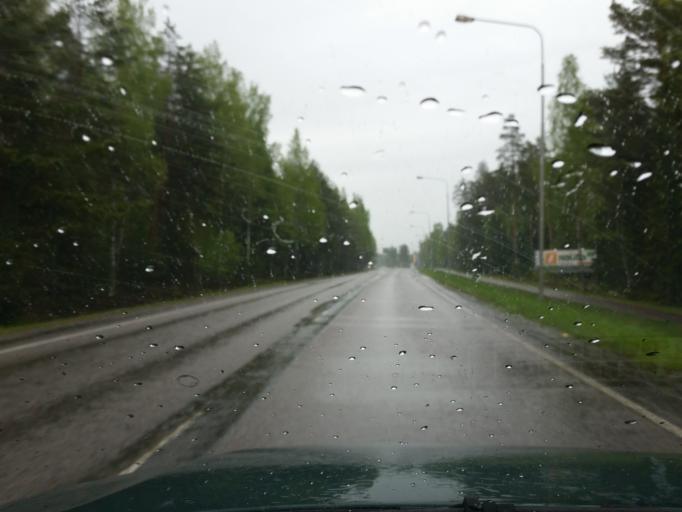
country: FI
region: Uusimaa
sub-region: Helsinki
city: Lohja
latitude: 60.2846
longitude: 24.1674
